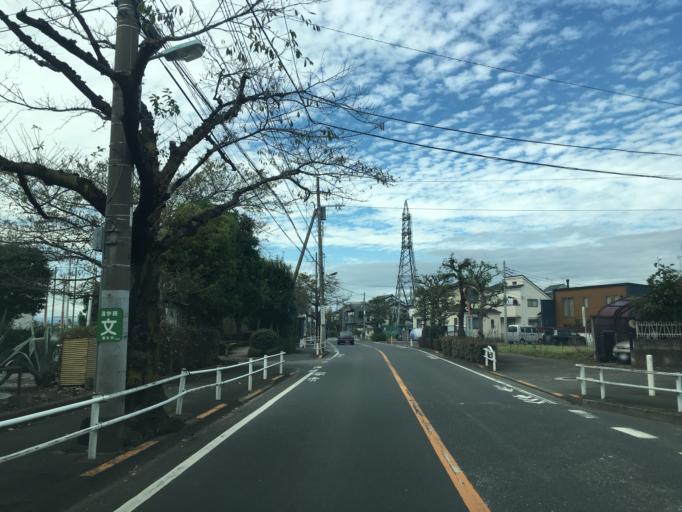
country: JP
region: Tokyo
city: Chofugaoka
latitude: 35.6406
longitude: 139.5475
